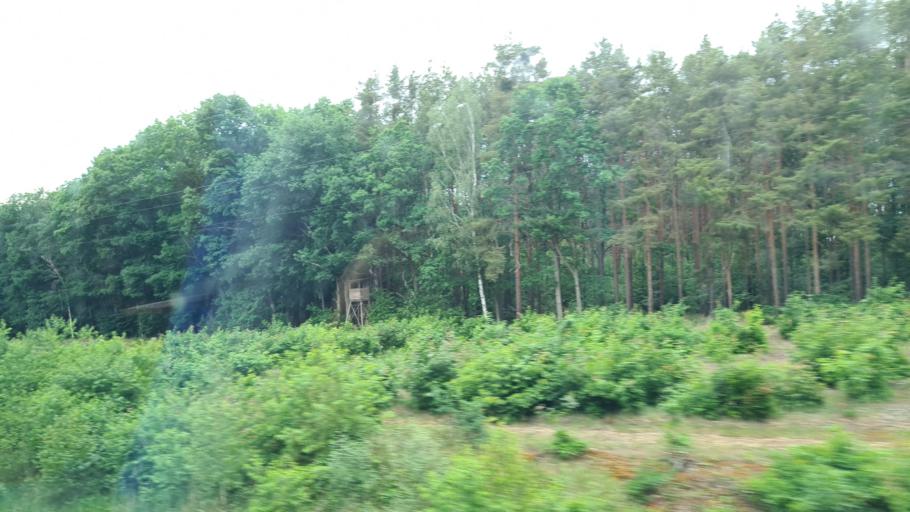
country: DE
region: Brandenburg
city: Falkenberg
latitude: 51.5866
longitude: 13.3118
